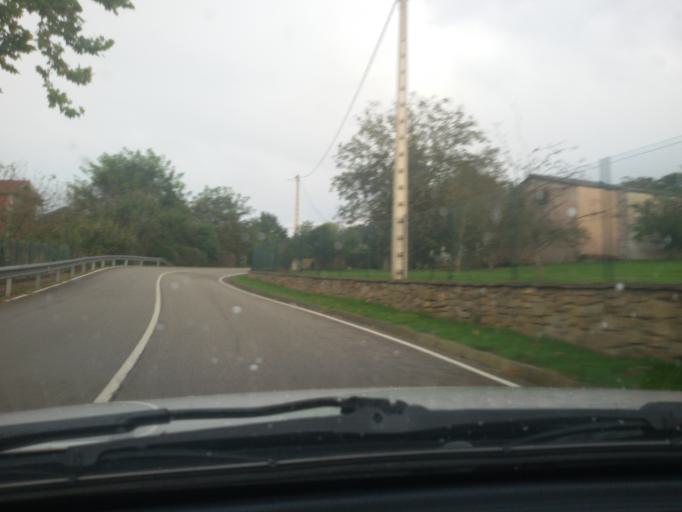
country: ES
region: Asturias
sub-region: Province of Asturias
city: Norena
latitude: 43.3705
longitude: -5.7537
